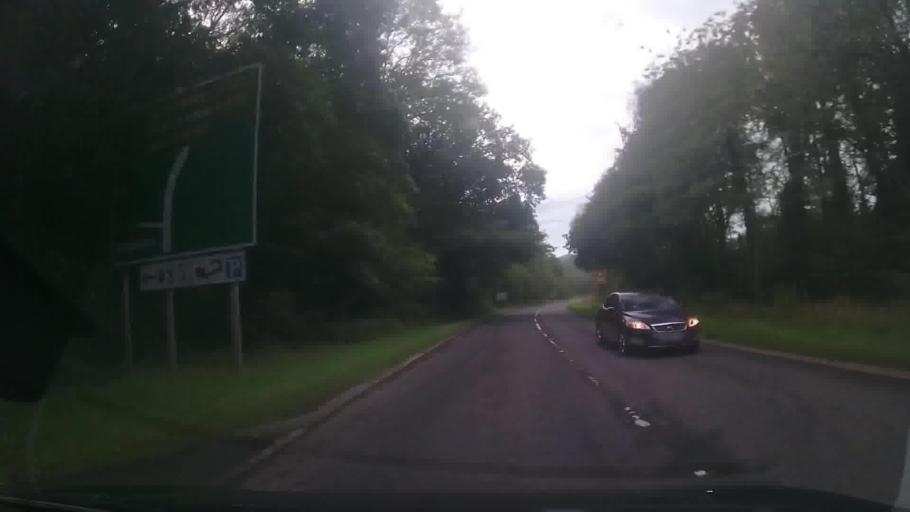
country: GB
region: Wales
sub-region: Gwynedd
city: Dolgellau
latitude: 52.7446
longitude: -3.8651
